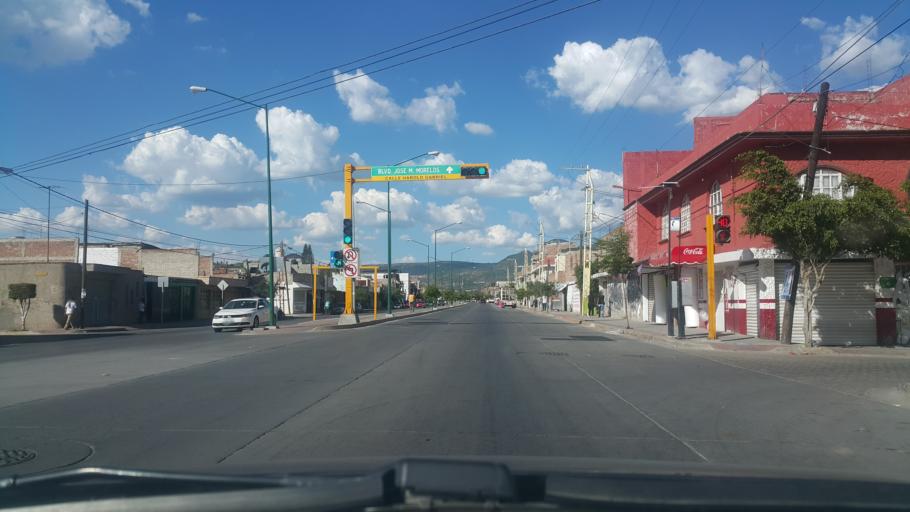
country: MX
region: Guanajuato
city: Leon
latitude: 21.1399
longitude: -101.6479
